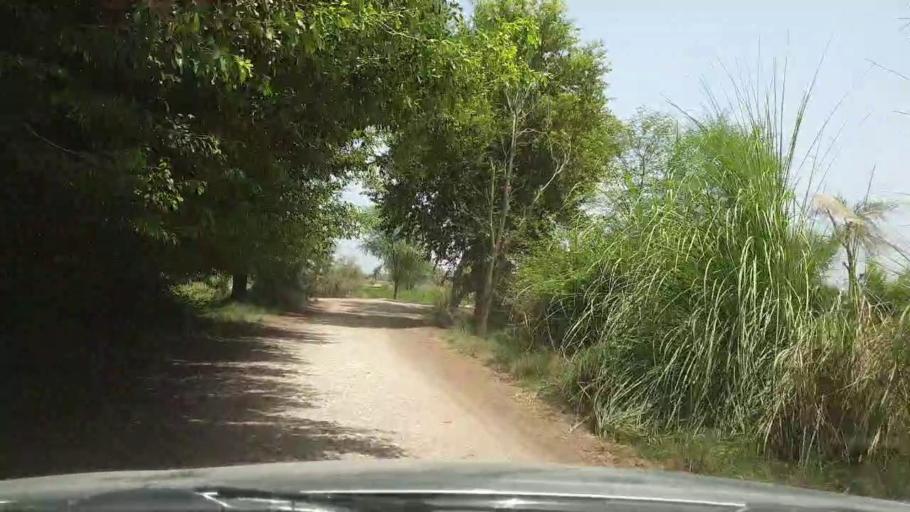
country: PK
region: Sindh
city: Pano Aqil
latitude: 27.8683
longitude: 69.1756
